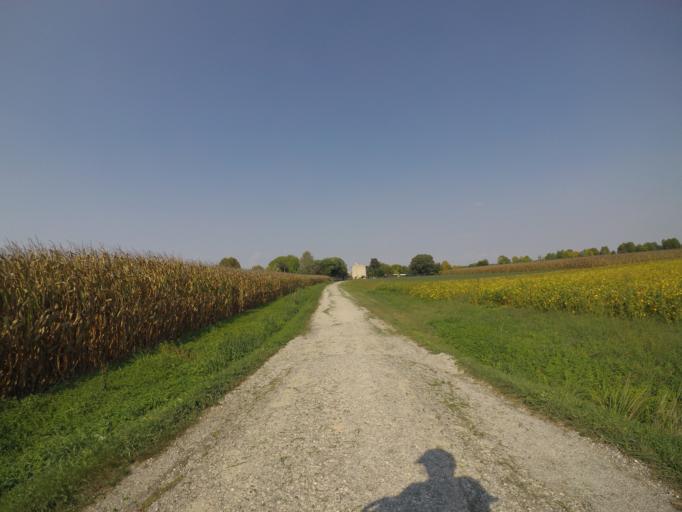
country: IT
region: Friuli Venezia Giulia
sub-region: Provincia di Udine
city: Camino al Tagliamento
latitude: 45.9143
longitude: 12.9285
